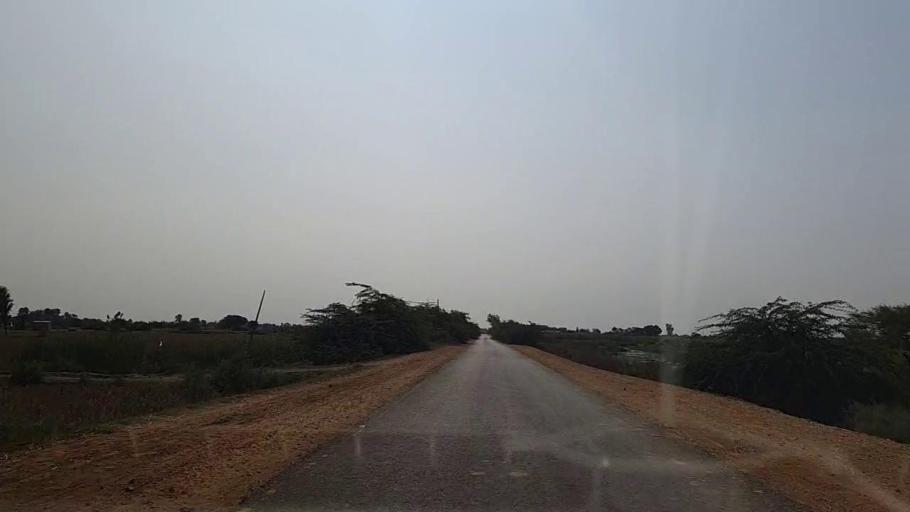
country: PK
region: Sindh
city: Chuhar Jamali
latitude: 24.3146
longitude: 67.9397
